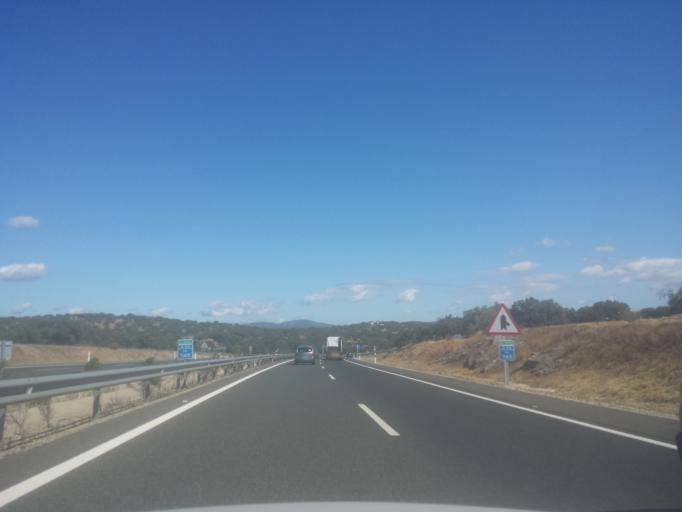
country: ES
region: Andalusia
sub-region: Provincia de Huelva
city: Santa Olalla del Cala
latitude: 37.9192
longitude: -6.2242
